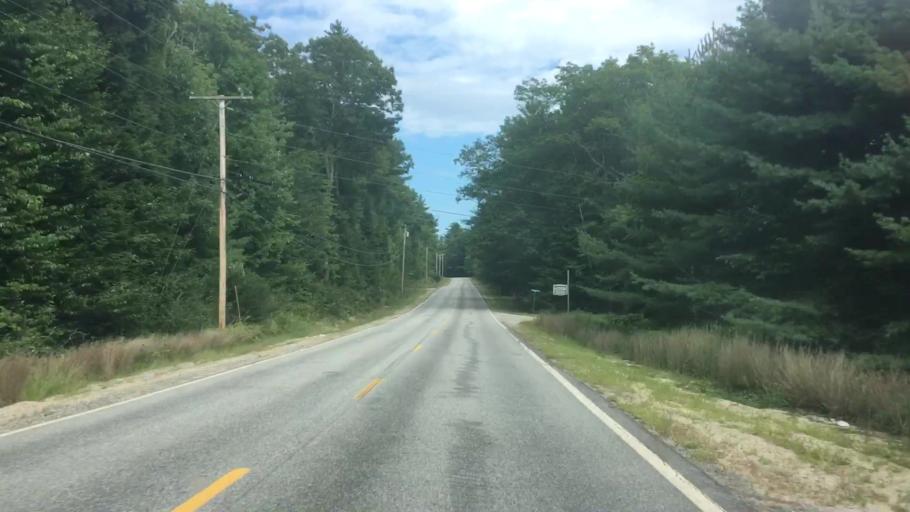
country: US
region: Maine
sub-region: Oxford County
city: Oxford
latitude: 44.0956
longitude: -70.5197
